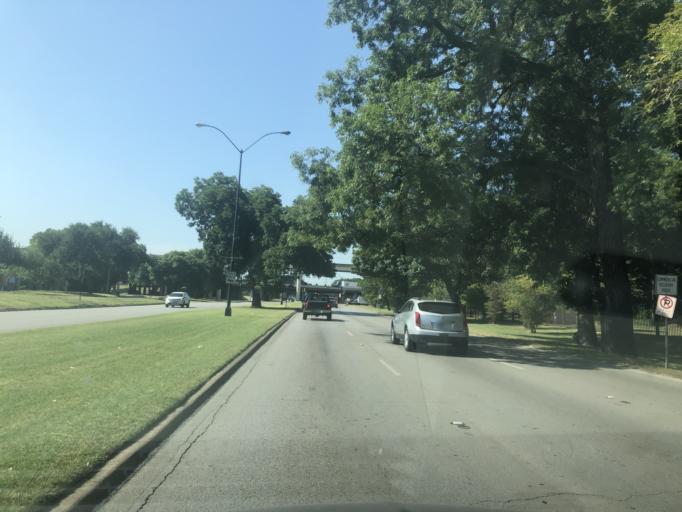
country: US
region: Texas
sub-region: Tarrant County
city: Fort Worth
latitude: 32.7358
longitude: -97.3614
